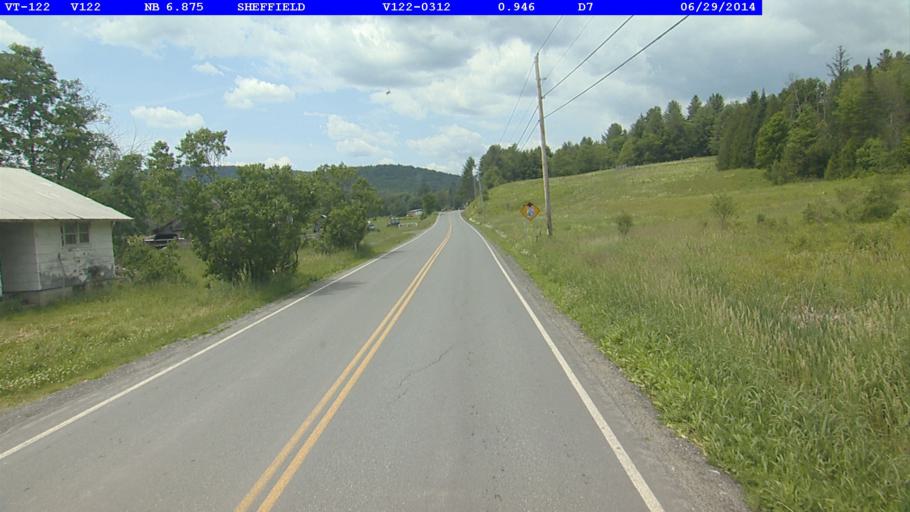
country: US
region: Vermont
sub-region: Caledonia County
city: Lyndonville
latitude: 44.5978
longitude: -72.1072
